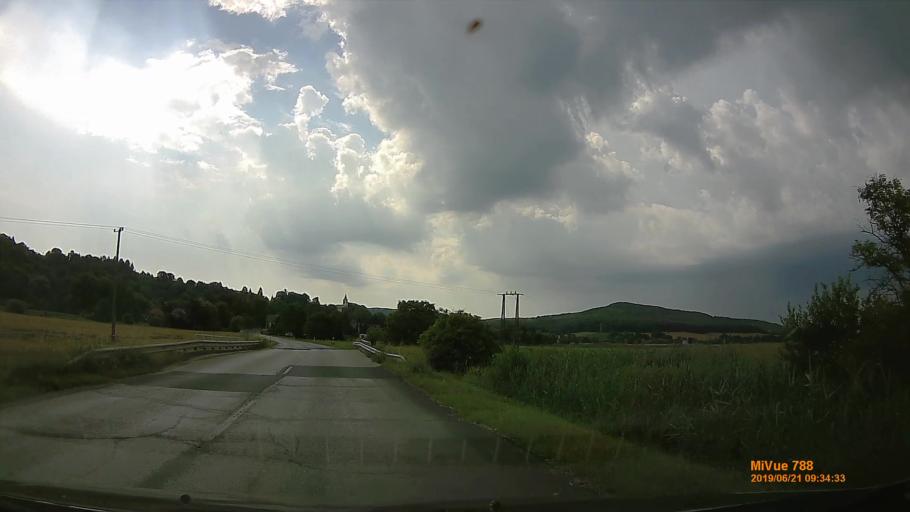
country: HU
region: Somogy
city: Taszar
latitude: 46.3258
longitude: 17.8881
